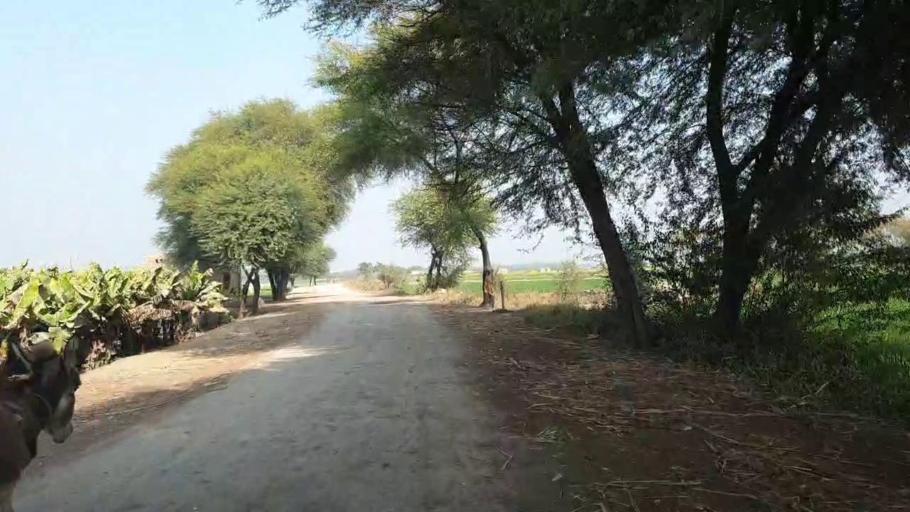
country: PK
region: Sindh
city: Bhit Shah
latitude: 25.7723
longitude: 68.5128
